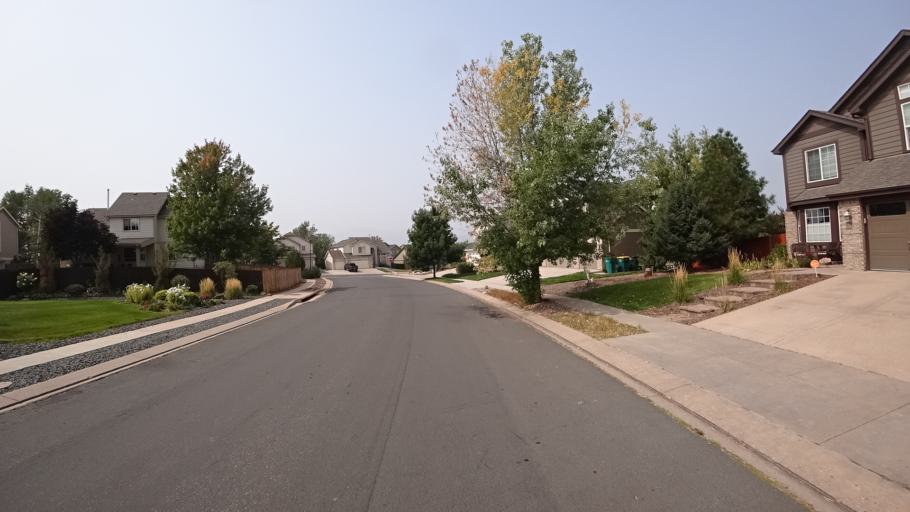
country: US
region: Colorado
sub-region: El Paso County
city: Cimarron Hills
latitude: 38.9270
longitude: -104.7463
